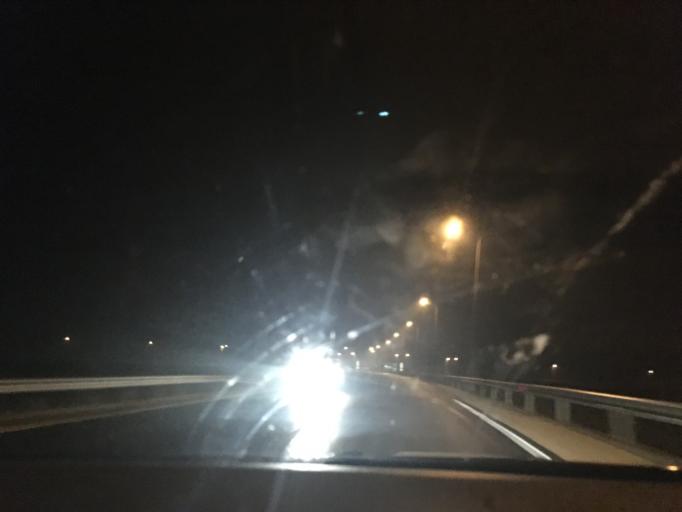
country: HU
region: Hajdu-Bihar
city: Hajduszoboszlo
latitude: 47.4107
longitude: 21.4083
